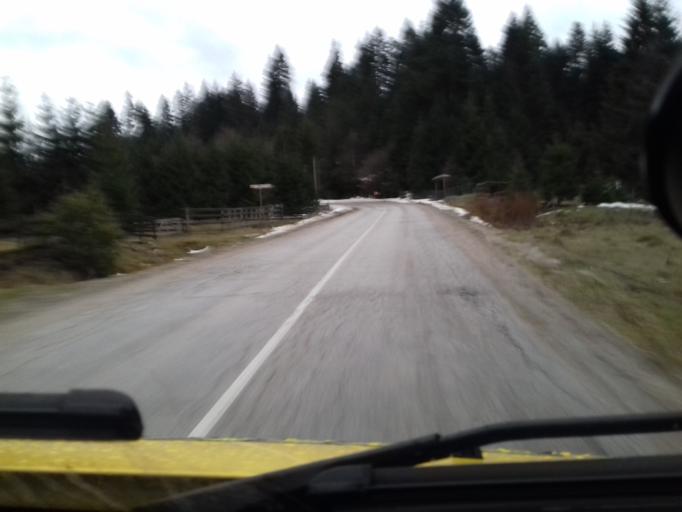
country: BA
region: Federation of Bosnia and Herzegovina
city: Turbe
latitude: 44.3073
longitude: 17.4911
